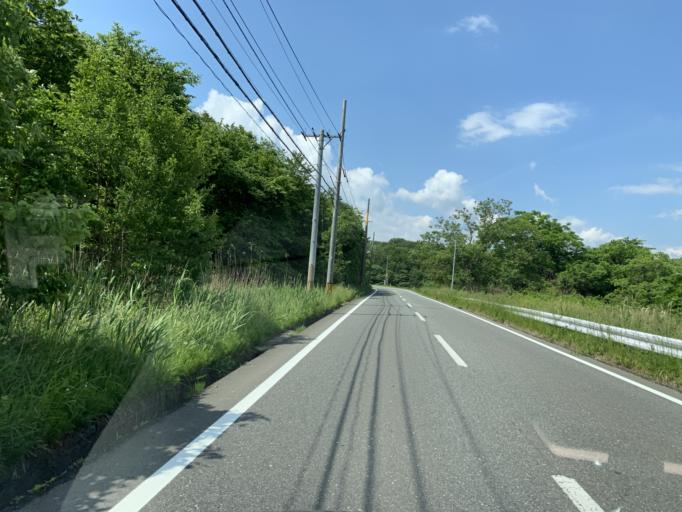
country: JP
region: Miyagi
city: Furukawa
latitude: 38.7242
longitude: 140.9498
